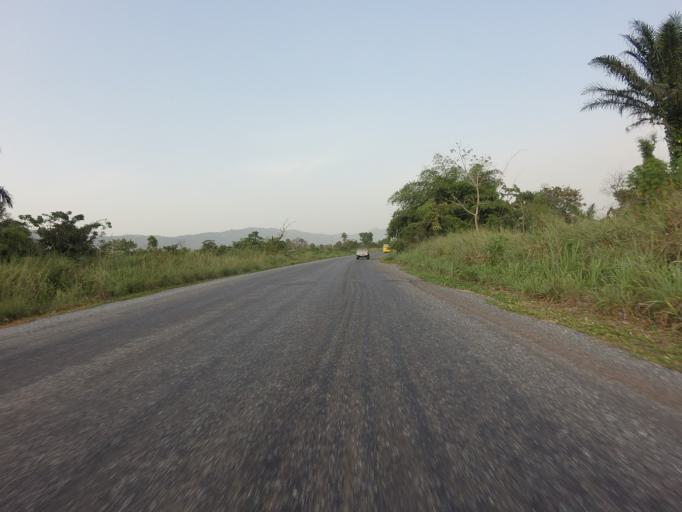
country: GH
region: Volta
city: Ho
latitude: 6.4647
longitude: 0.2216
